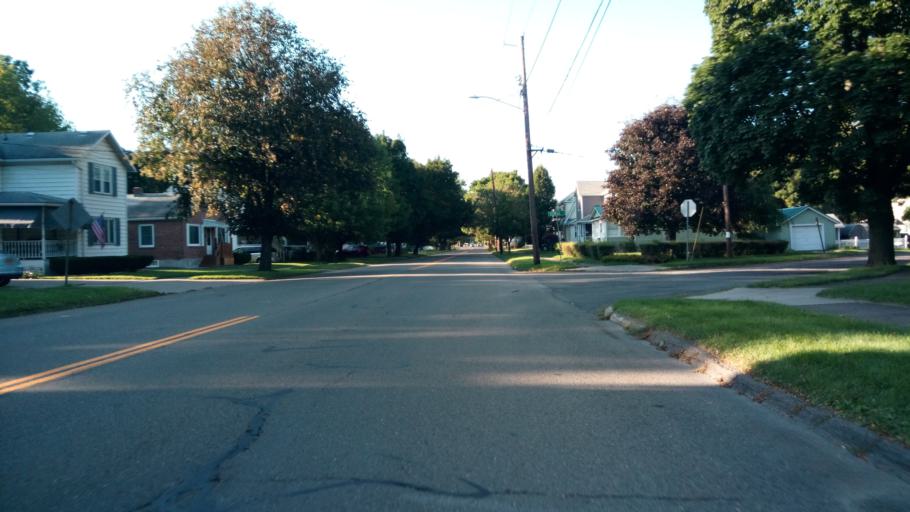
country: US
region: New York
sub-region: Chemung County
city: Elmira Heights
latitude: 42.1117
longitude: -76.8264
